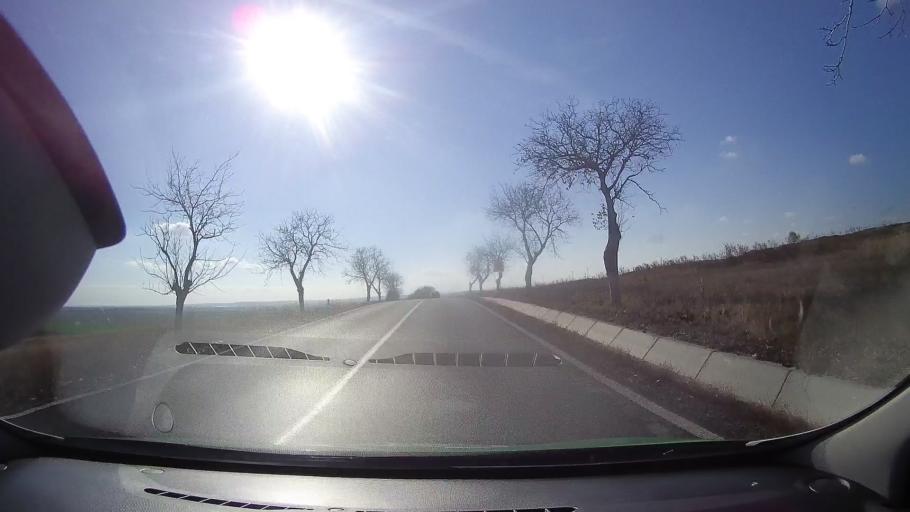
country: RO
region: Tulcea
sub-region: Comuna Ceamurlia de Jos
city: Ceamurlia de Jos
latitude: 44.8073
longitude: 28.6911
